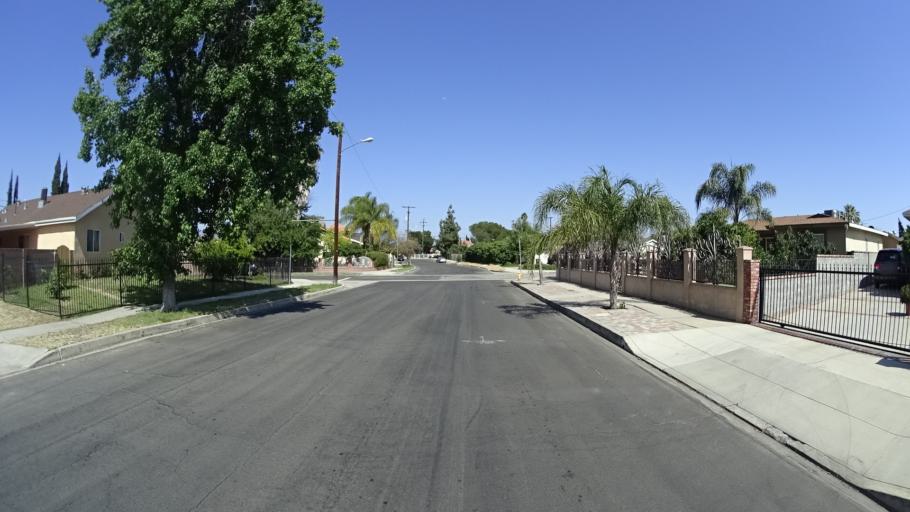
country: US
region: California
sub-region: Los Angeles County
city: Van Nuys
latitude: 34.2181
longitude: -118.4160
